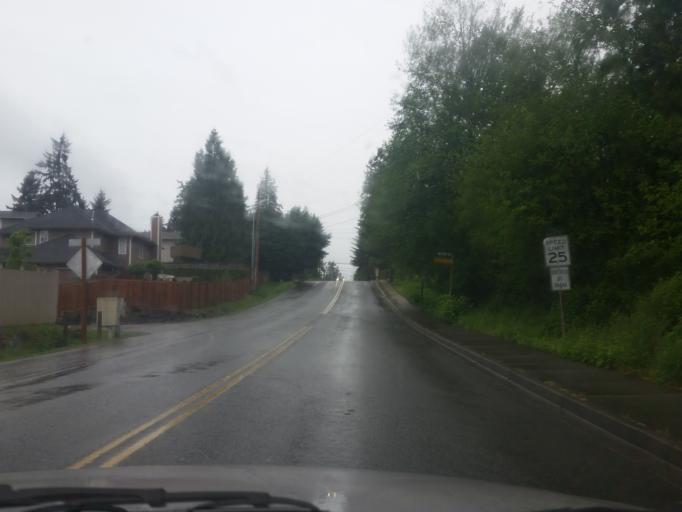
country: US
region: Washington
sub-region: King County
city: Inglewood-Finn Hill
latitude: 47.7406
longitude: -122.2262
